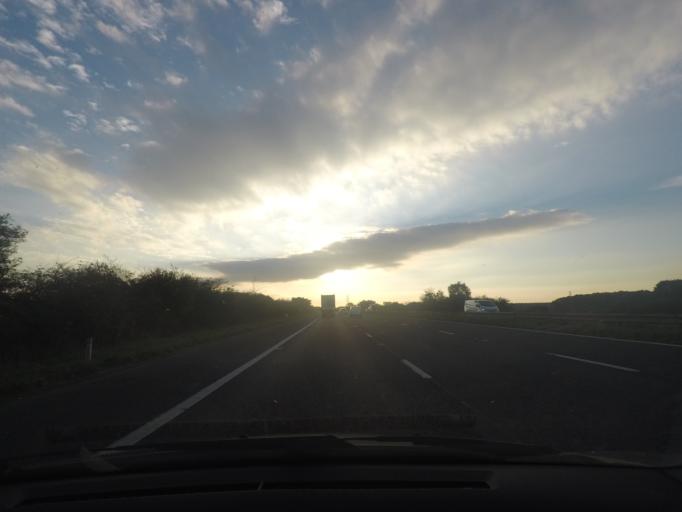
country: GB
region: England
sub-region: North Lincolnshire
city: Brigg
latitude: 53.5589
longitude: -0.5006
